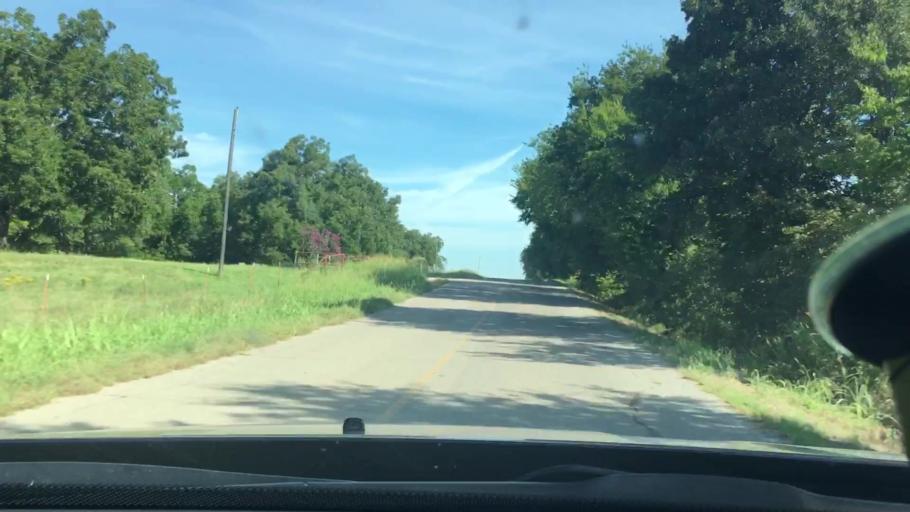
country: US
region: Oklahoma
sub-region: Carter County
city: Lone Grove
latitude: 34.2938
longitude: -97.2824
